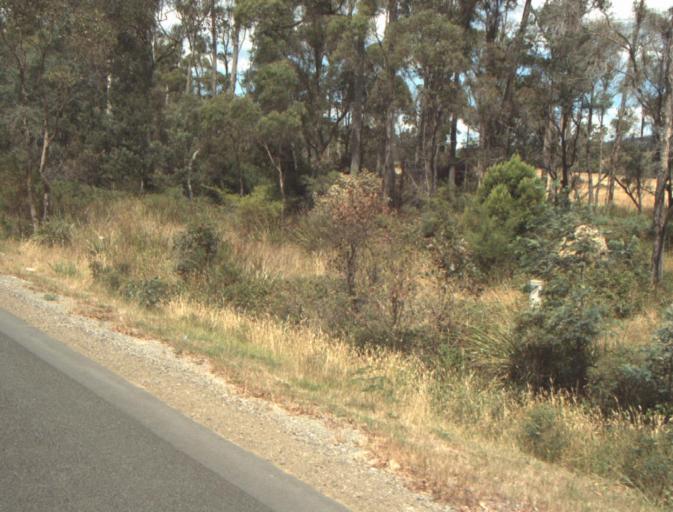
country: AU
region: Tasmania
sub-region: Launceston
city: Mayfield
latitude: -41.2297
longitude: 147.1448
